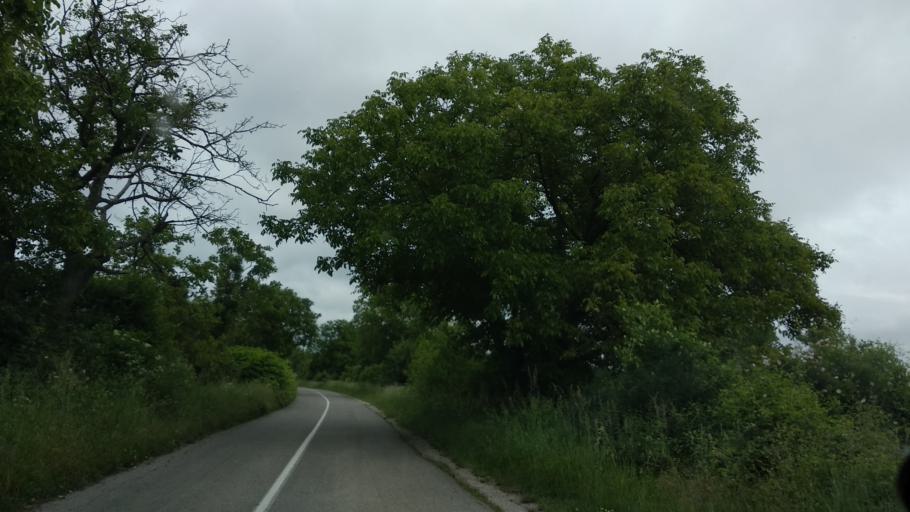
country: SK
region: Nitriansky
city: Trencianske Teplice
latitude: 48.7880
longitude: 18.1430
